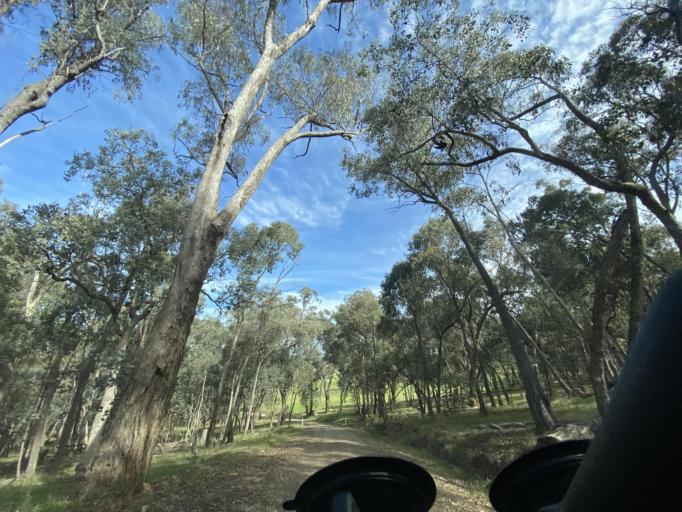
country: AU
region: Victoria
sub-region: Mansfield
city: Mansfield
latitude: -36.8041
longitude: 146.1217
